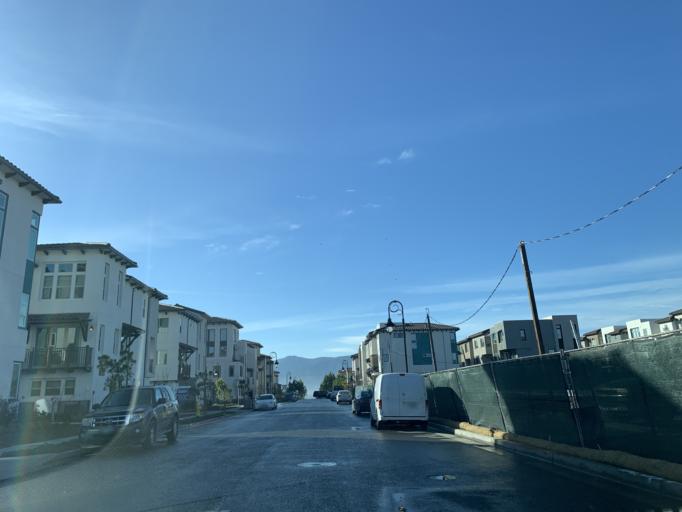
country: US
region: California
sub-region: Santa Clara County
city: Seven Trees
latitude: 37.2850
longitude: -121.8543
